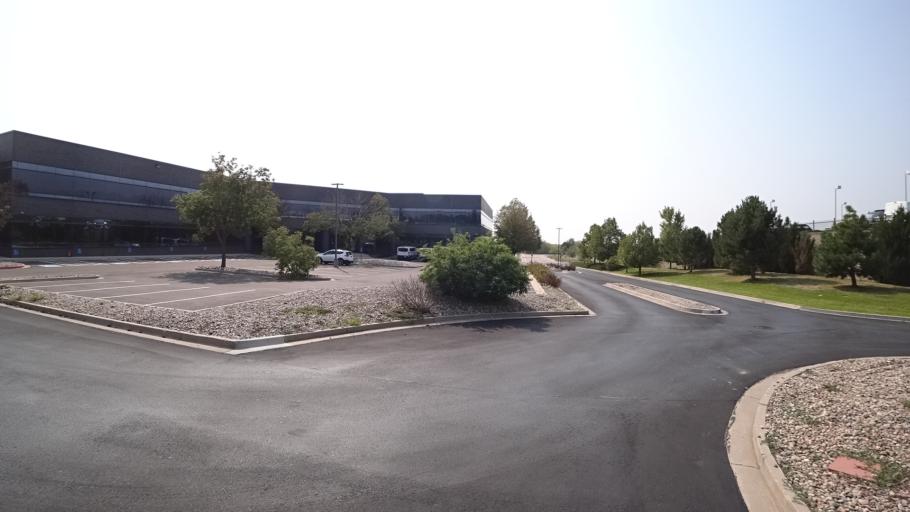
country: US
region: Colorado
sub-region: El Paso County
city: Stratmoor
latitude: 38.8126
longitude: -104.7551
